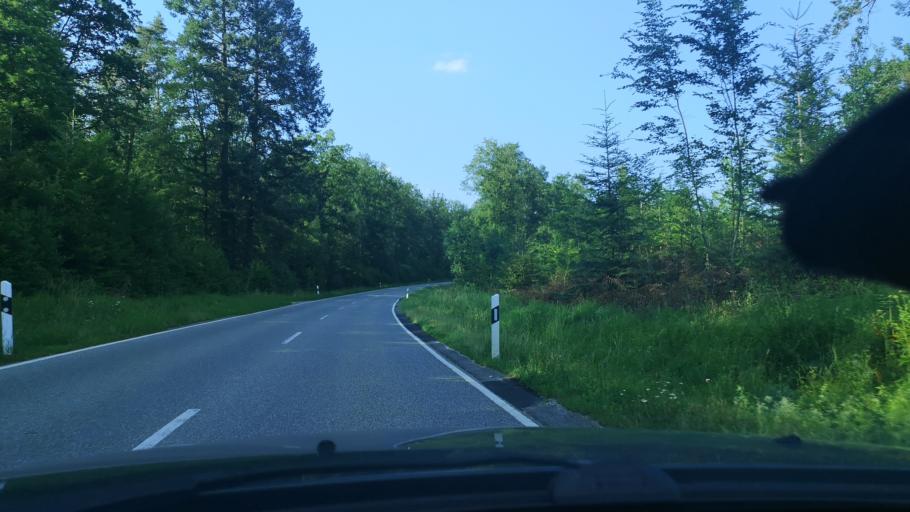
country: DE
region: Baden-Wuerttemberg
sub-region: Regierungsbezirk Stuttgart
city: Schlat
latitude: 48.6640
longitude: 9.7224
